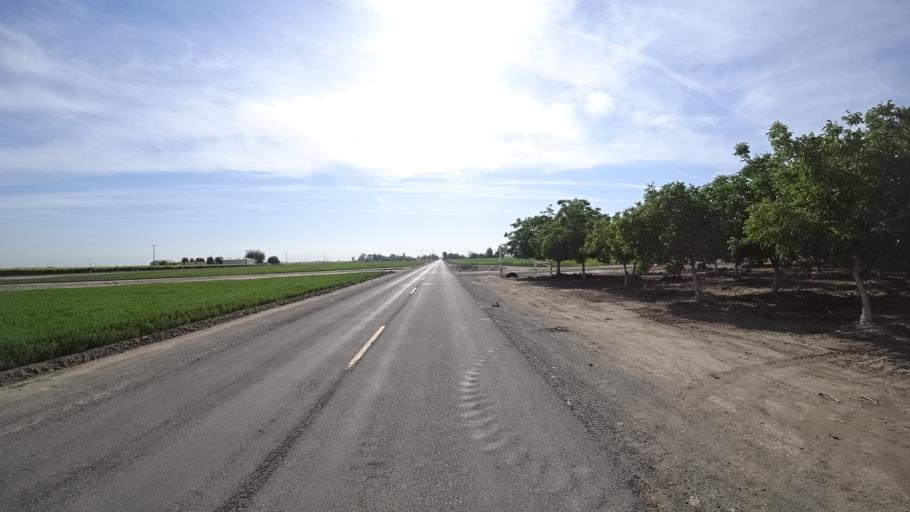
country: US
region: California
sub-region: Tulare County
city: Goshen
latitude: 36.3492
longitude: -119.4849
